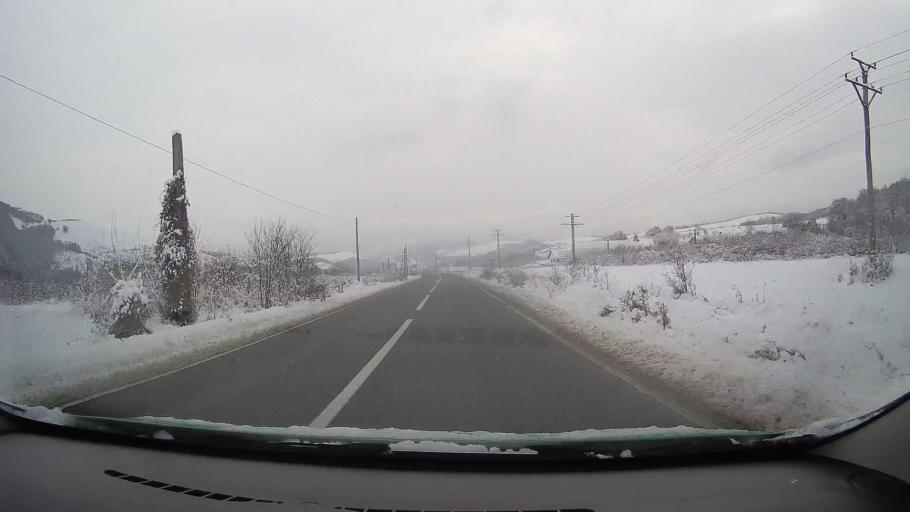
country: RO
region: Alba
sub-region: Comuna Sasciori
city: Sebesel
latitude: 45.9027
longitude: 23.5575
